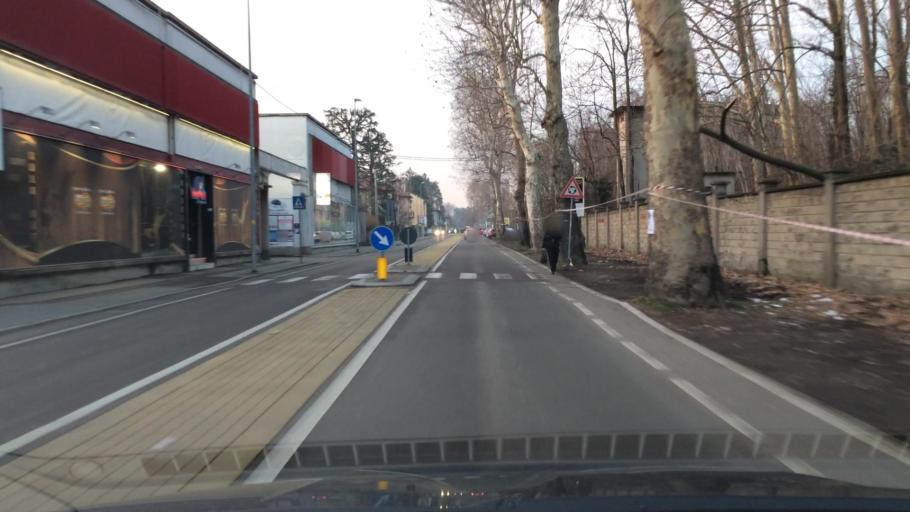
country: IT
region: Lombardy
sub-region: Provincia di Varese
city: Saronno
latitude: 45.6204
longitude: 9.0293
